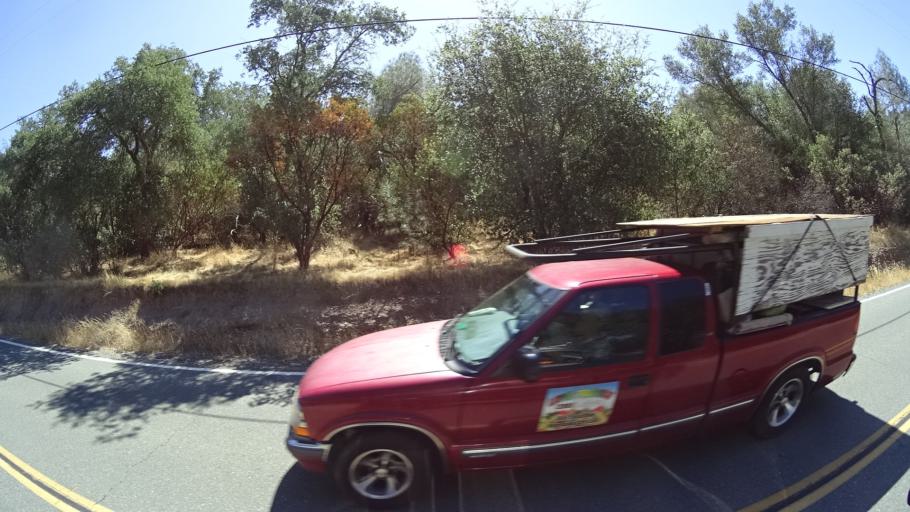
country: US
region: California
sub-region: Calaveras County
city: Valley Springs
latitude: 38.2063
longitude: -120.8794
